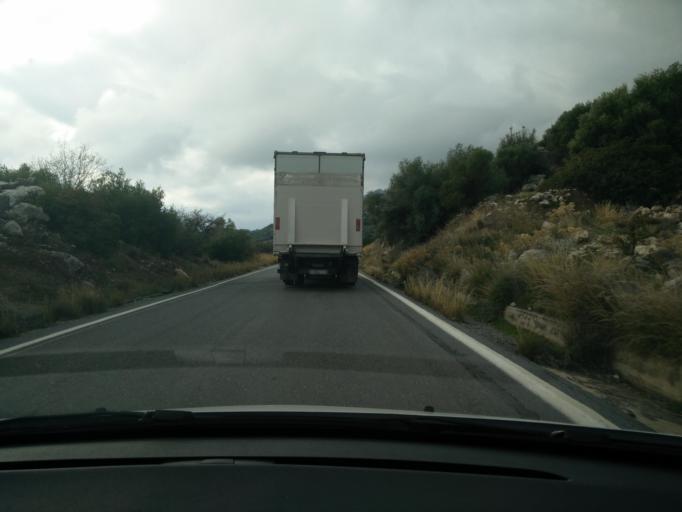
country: GR
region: Crete
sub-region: Nomos Lasithiou
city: Gra Liyia
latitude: 35.0220
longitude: 25.5567
